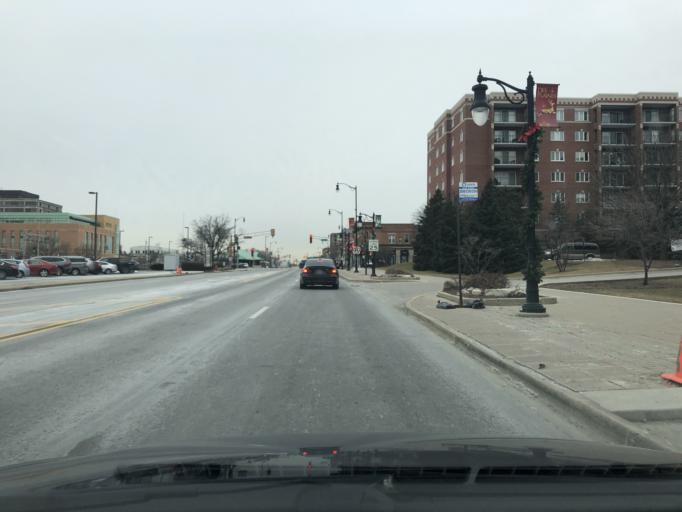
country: US
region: Illinois
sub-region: Cook County
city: Des Plaines
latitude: 42.0401
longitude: -87.8842
